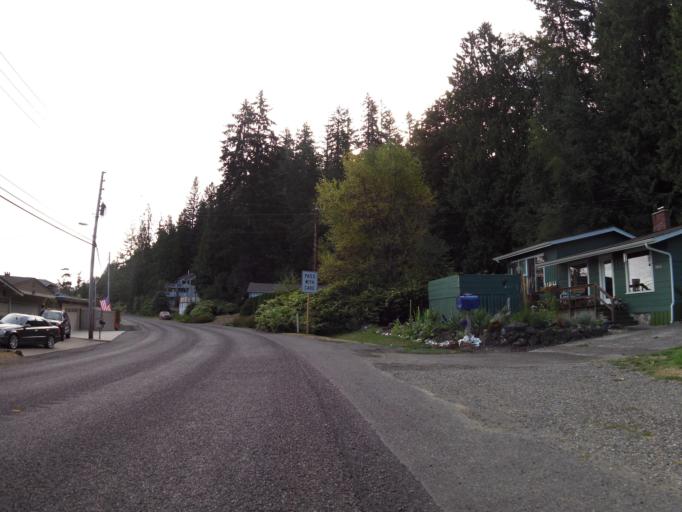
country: US
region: Washington
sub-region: Mason County
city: Allyn
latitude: 47.3823
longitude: -122.9423
